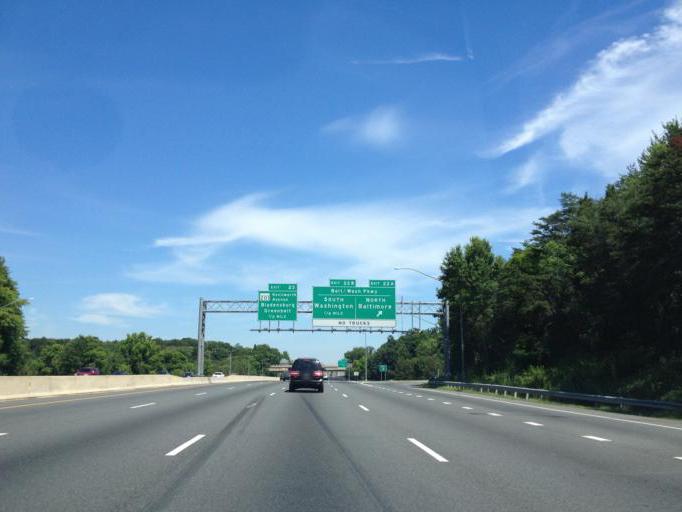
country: US
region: Maryland
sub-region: Prince George's County
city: Greenbelt
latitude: 38.9884
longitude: -76.8830
